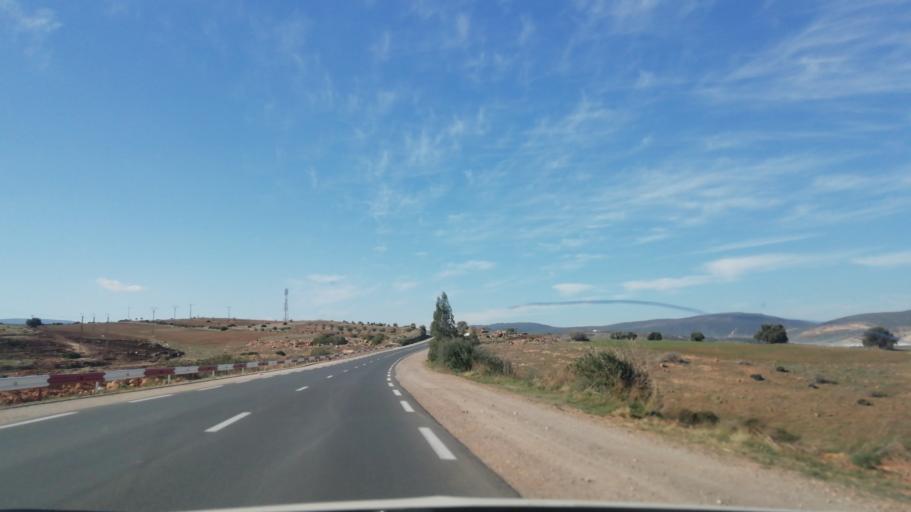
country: DZ
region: Tlemcen
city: Ouled Mimoun
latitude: 34.8769
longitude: -1.1117
